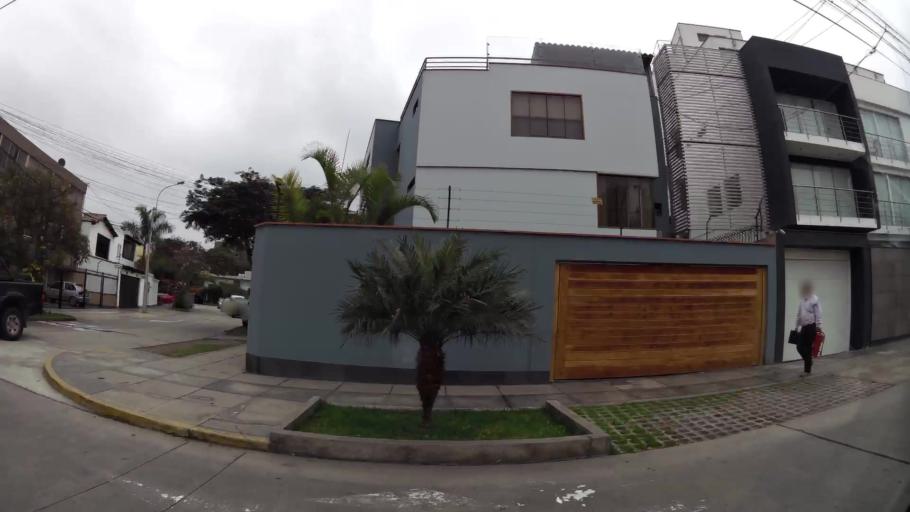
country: PE
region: Lima
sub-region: Lima
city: Surco
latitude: -12.1285
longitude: -77.0158
